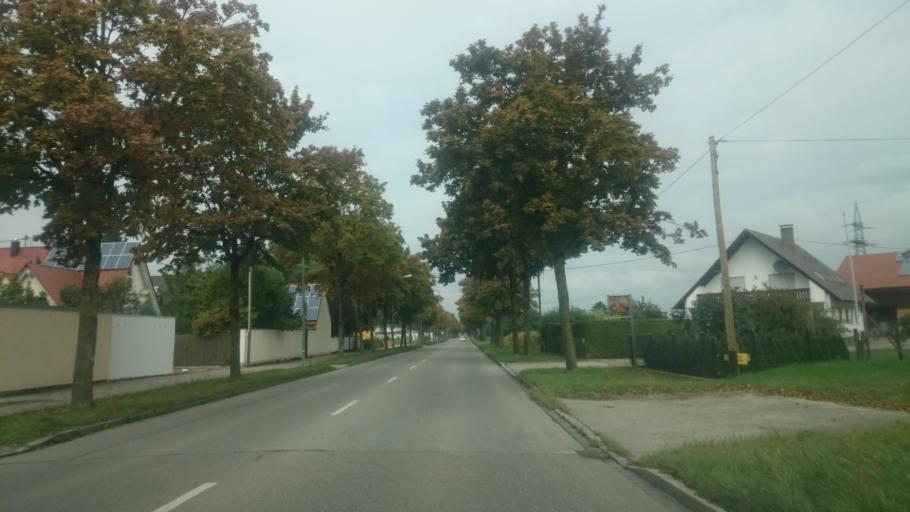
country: DE
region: Bavaria
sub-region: Swabia
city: Friedberg
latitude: 48.3662
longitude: 10.9474
